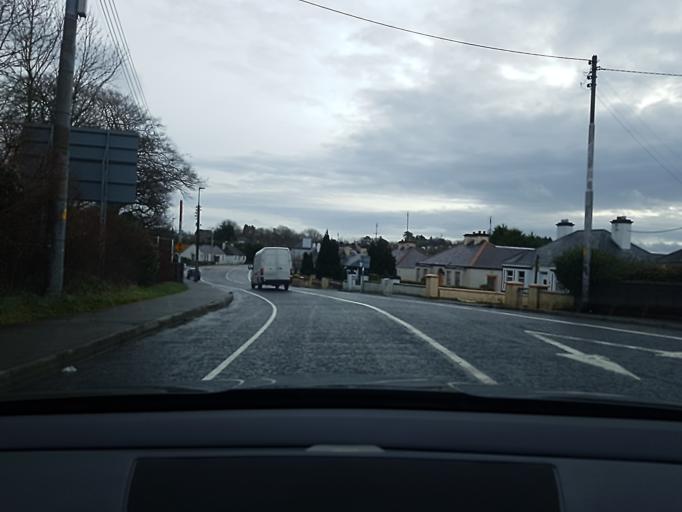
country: IE
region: Connaught
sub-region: Maigh Eo
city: Castlebar
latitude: 53.8509
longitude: -9.2920
